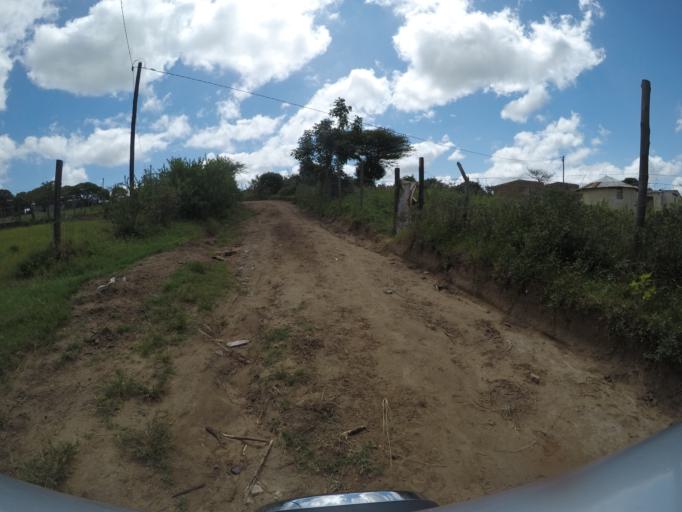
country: ZA
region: KwaZulu-Natal
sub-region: uThungulu District Municipality
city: Empangeni
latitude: -28.5873
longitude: 31.8404
